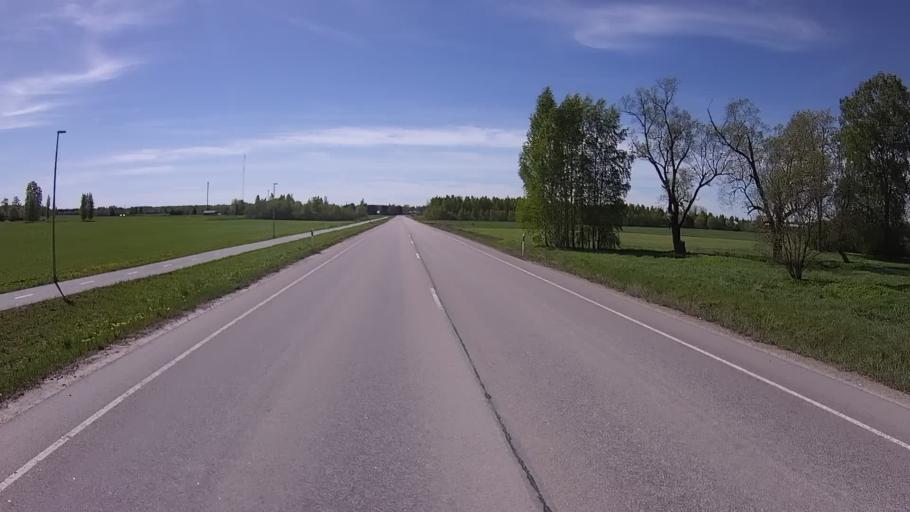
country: EE
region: Polvamaa
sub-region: Polva linn
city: Polva
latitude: 58.0798
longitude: 27.0896
